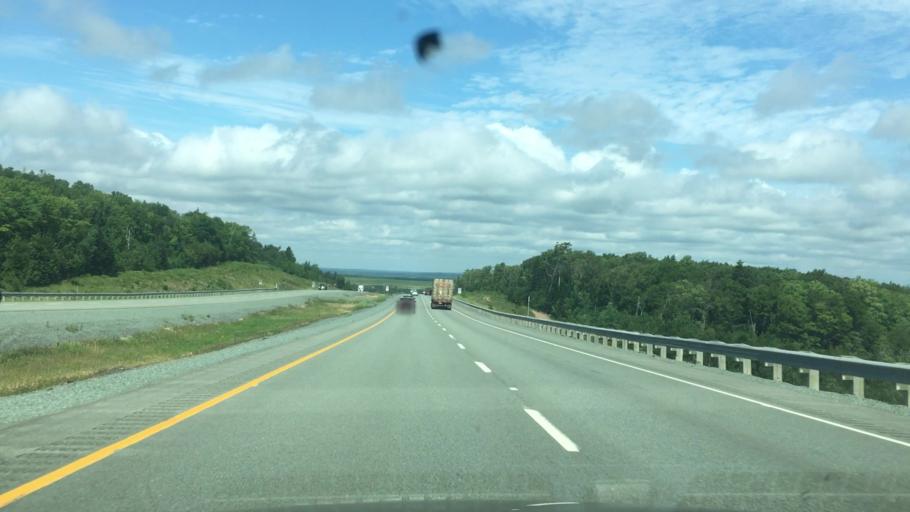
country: CA
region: Nova Scotia
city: Oxford
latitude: 45.5905
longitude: -63.7234
